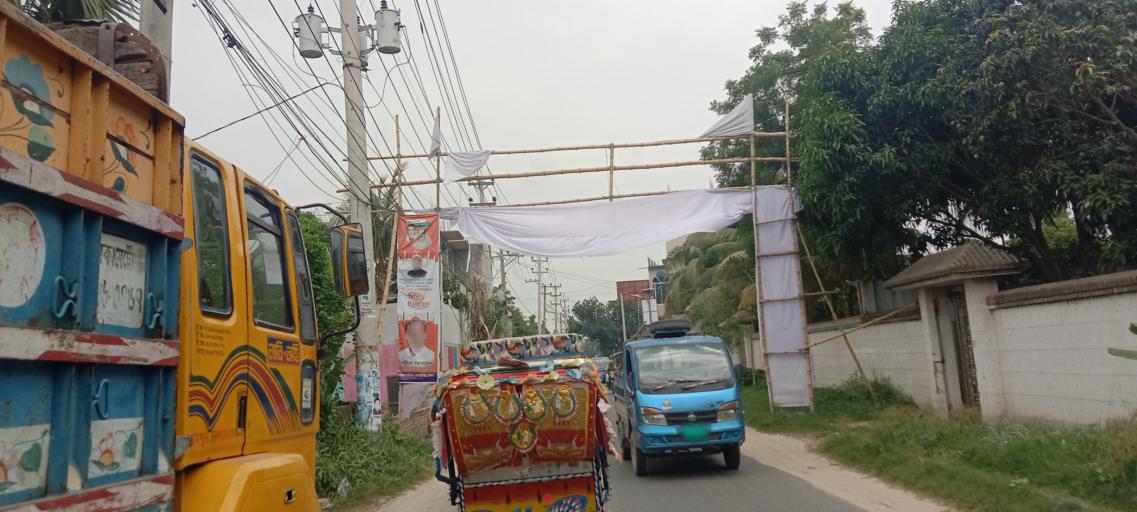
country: BD
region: Dhaka
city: Azimpur
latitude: 23.7096
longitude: 90.3470
